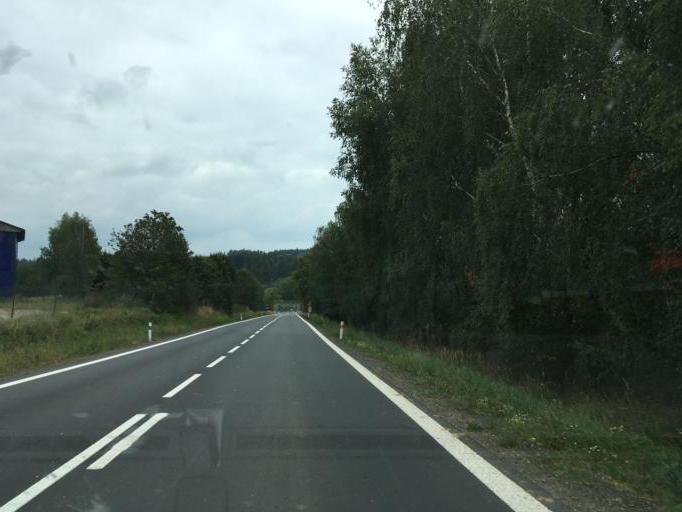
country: CZ
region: Central Bohemia
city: Cechtice
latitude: 49.5552
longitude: 15.1221
